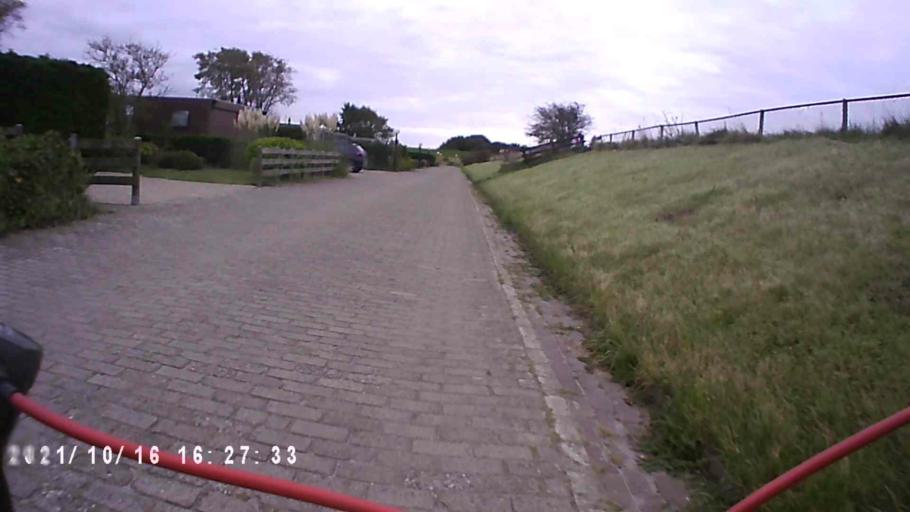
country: NL
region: Friesland
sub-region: Gemeente Dongeradeel
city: Anjum
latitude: 53.3838
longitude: 6.1561
